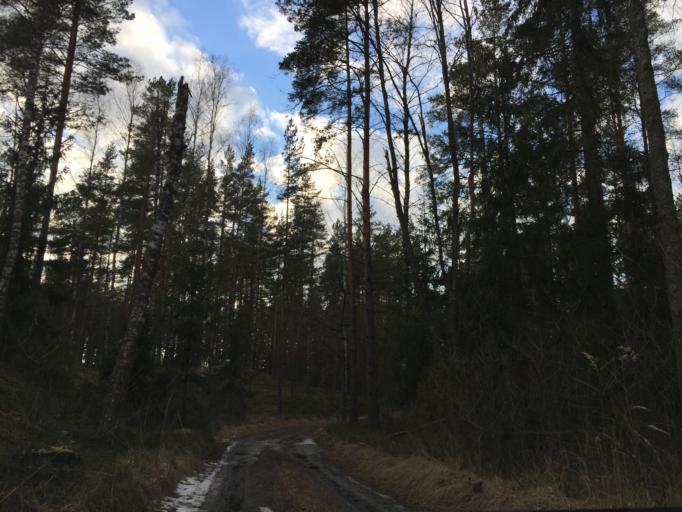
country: LV
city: Tireli
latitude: 56.8639
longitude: 23.6284
